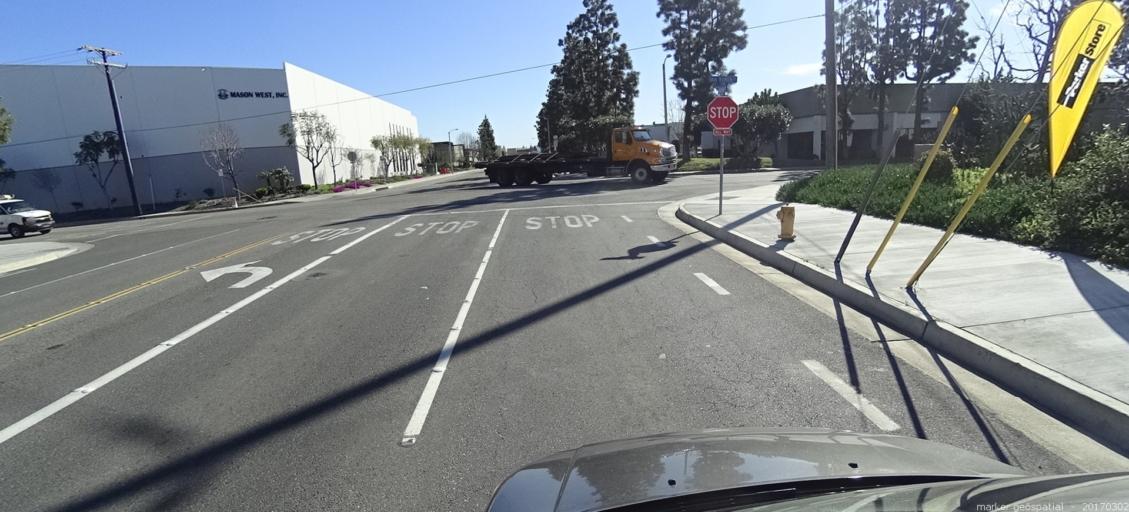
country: US
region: California
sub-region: Orange County
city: Yorba Linda
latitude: 33.8628
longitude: -117.8316
